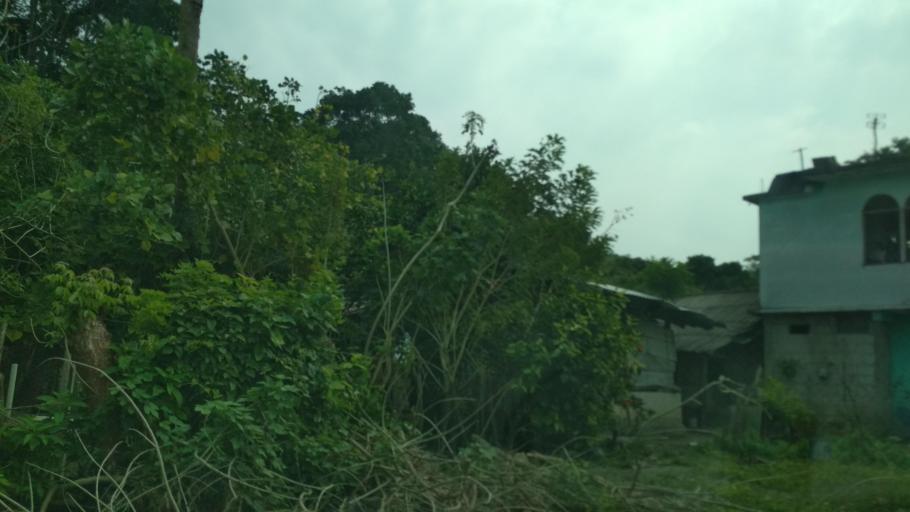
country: MM
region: Kayah
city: Loikaw
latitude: 20.2115
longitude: 97.3013
